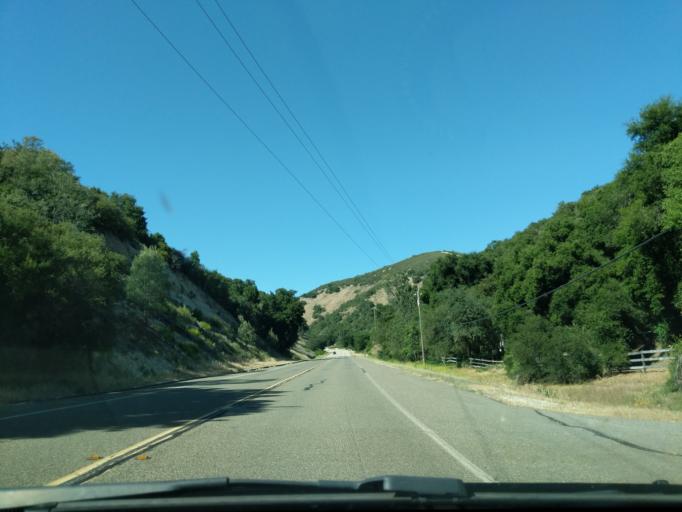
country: US
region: California
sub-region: Monterey County
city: King City
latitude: 36.0703
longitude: -121.1829
